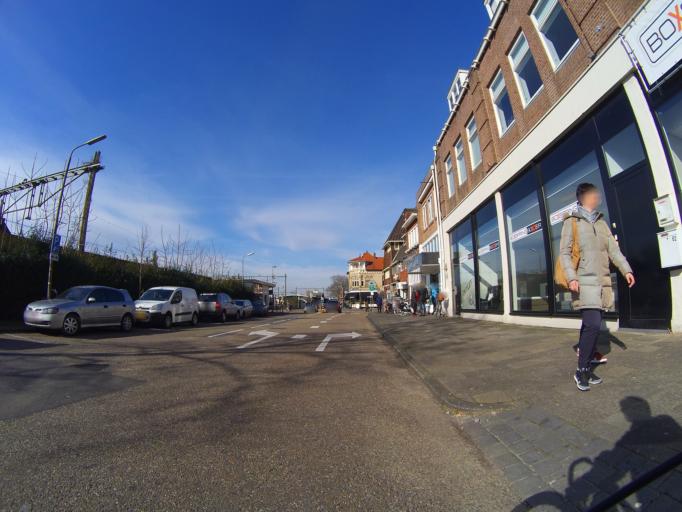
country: NL
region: North Holland
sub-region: Gemeente Bussum
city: Bussum
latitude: 52.2785
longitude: 5.1583
